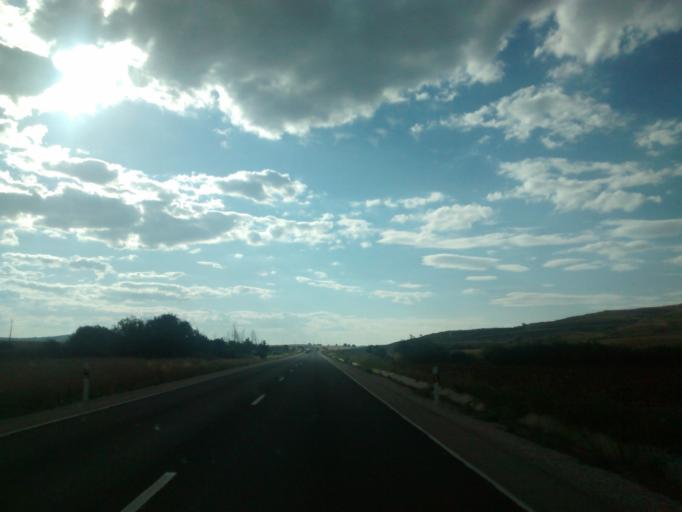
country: ES
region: Castille and Leon
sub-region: Provincia de Burgos
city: Basconcillos del Tozo
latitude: 42.6598
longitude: -3.9102
